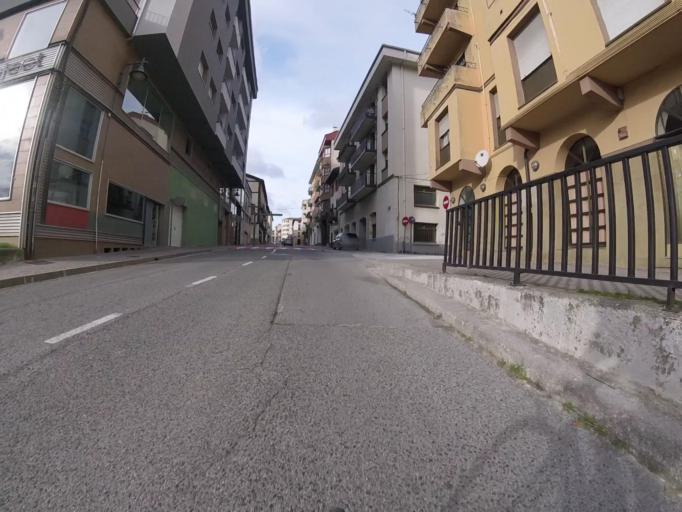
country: ES
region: Navarre
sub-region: Provincia de Navarra
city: Altsasu
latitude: 42.8937
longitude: -2.1672
